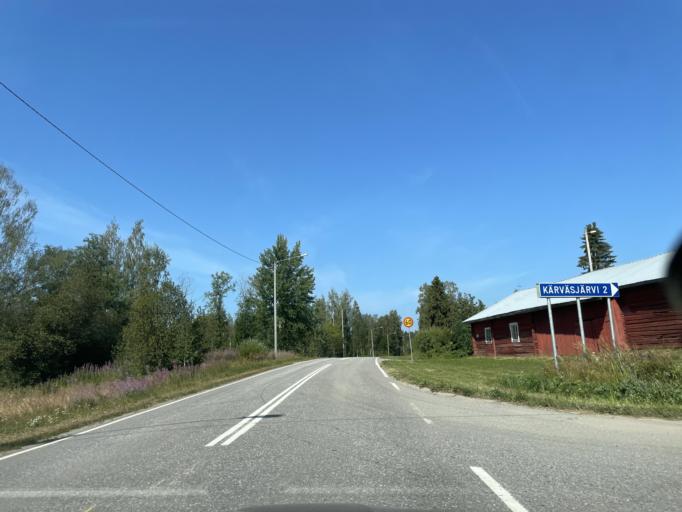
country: FI
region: Central Finland
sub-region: Saarijaervi-Viitasaari
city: Pihtipudas
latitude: 63.3584
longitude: 25.7515
